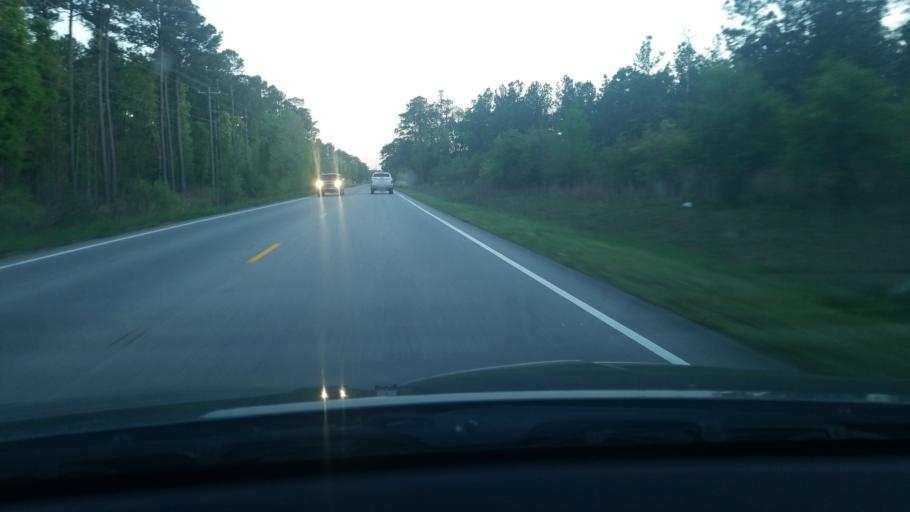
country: US
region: North Carolina
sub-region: Craven County
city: Vanceboro
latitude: 35.2235
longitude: -77.1198
